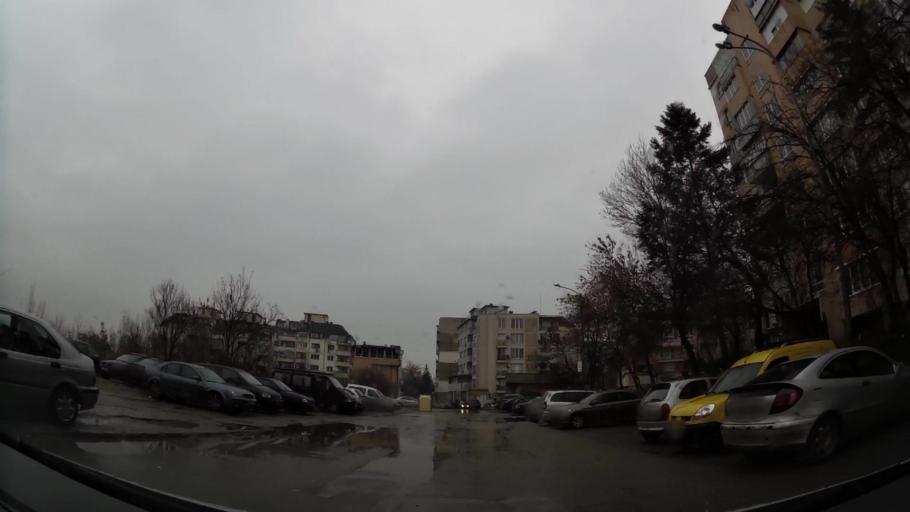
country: BG
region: Sofia-Capital
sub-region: Stolichna Obshtina
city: Sofia
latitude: 42.6407
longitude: 23.3662
